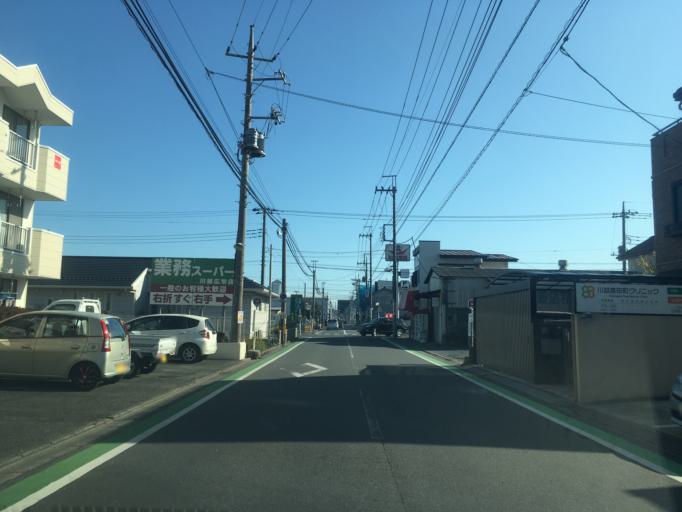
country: JP
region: Saitama
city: Kawagoe
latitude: 35.9031
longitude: 139.4663
